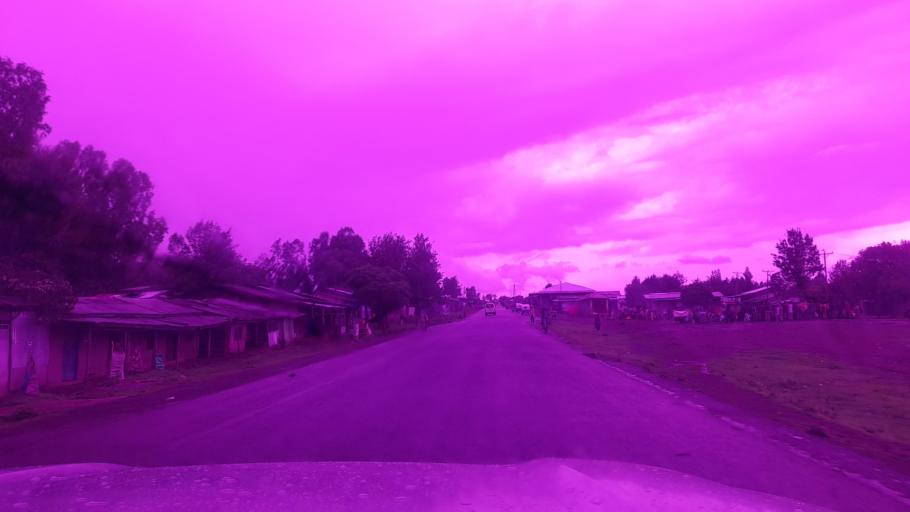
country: ET
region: Oromiya
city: Jima
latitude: 7.7148
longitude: 37.0930
